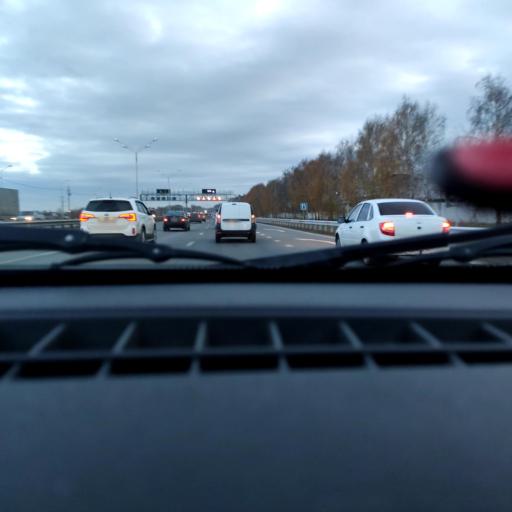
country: RU
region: Bashkortostan
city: Ufa
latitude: 54.5859
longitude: 55.9121
